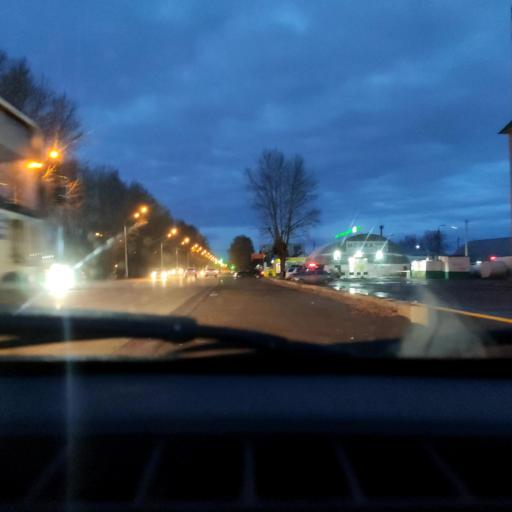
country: RU
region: Bashkortostan
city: Mikhaylovka
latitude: 54.6987
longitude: 55.8354
